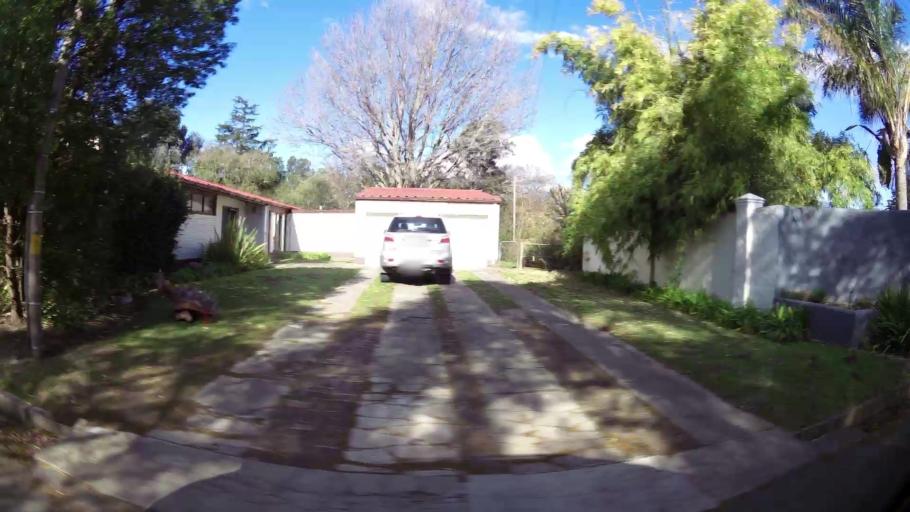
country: ZA
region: Western Cape
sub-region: Overberg District Municipality
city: Swellendam
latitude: -34.0246
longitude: 20.4420
